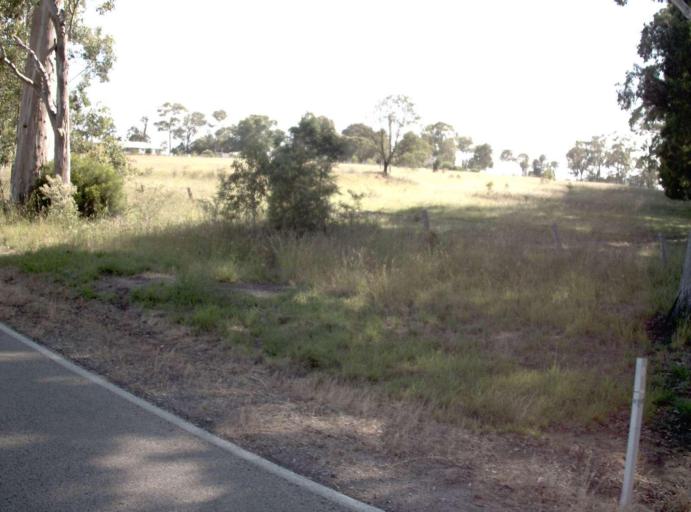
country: AU
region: Victoria
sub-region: East Gippsland
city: Lakes Entrance
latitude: -37.7678
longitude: 147.8127
